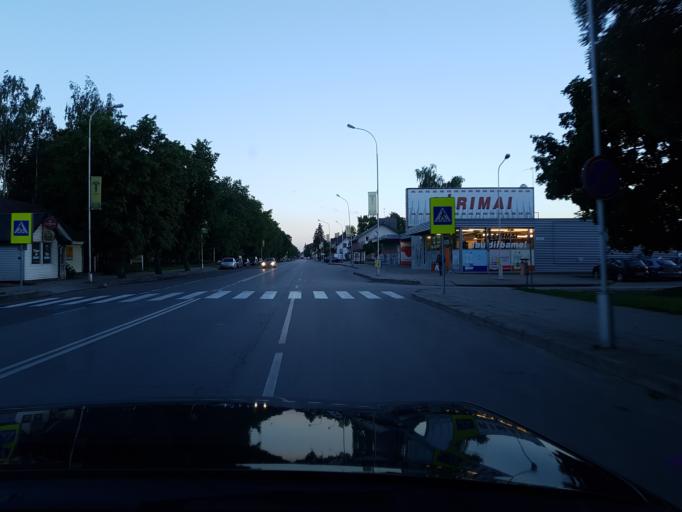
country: LT
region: Marijampoles apskritis
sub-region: Marijampole Municipality
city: Marijampole
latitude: 54.5668
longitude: 23.3589
